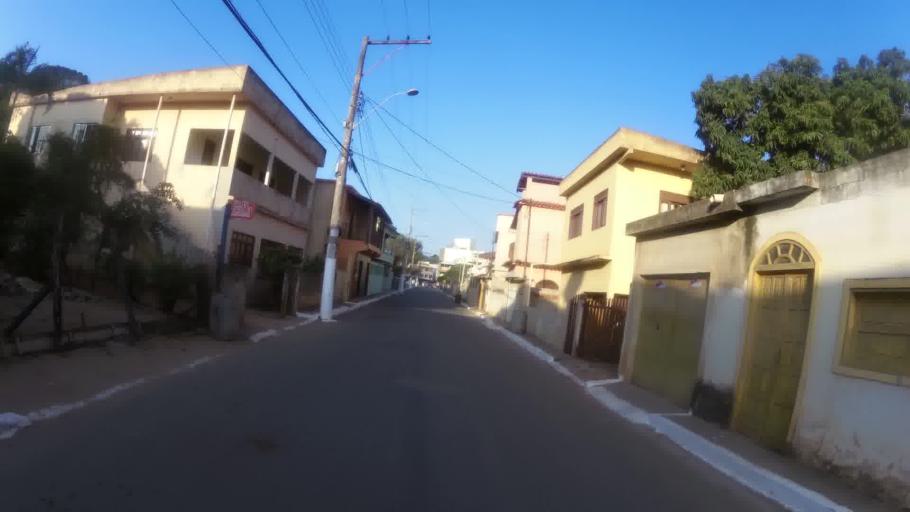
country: BR
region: Espirito Santo
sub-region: Piuma
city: Piuma
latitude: -20.8890
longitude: -40.7760
